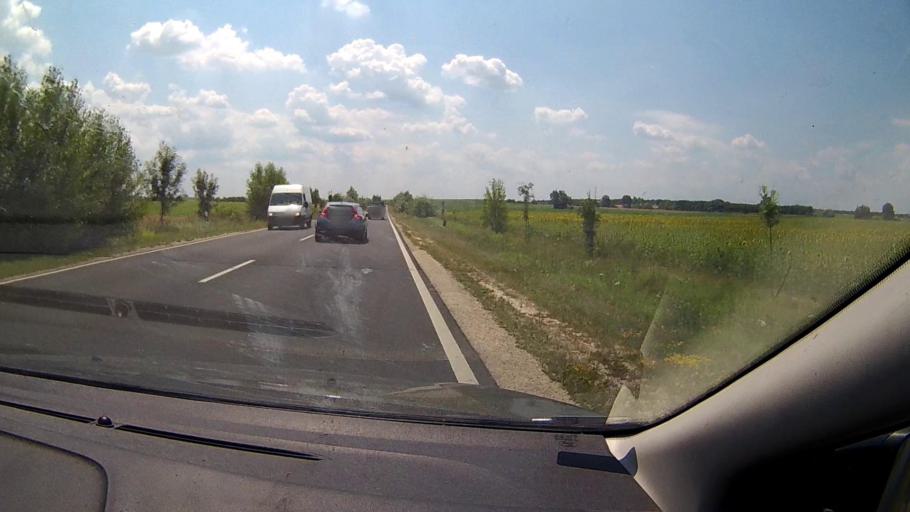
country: HU
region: Komarom-Esztergom
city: Tata
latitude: 47.6101
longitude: 18.3175
